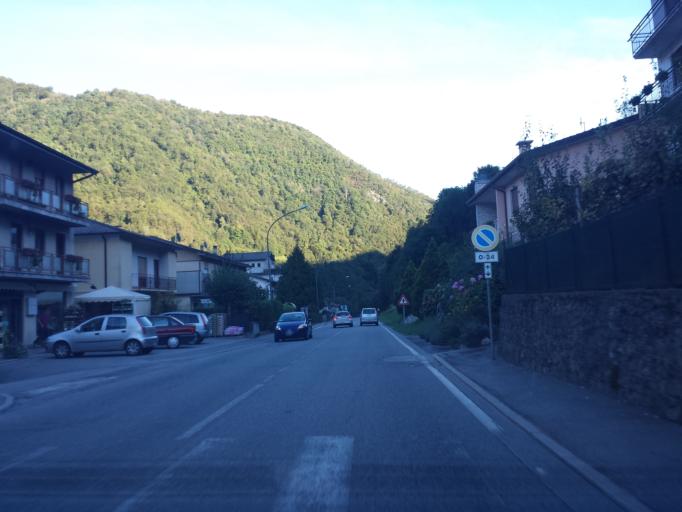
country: IT
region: Veneto
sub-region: Provincia di Vicenza
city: San Quirico
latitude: 45.6868
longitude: 11.2653
